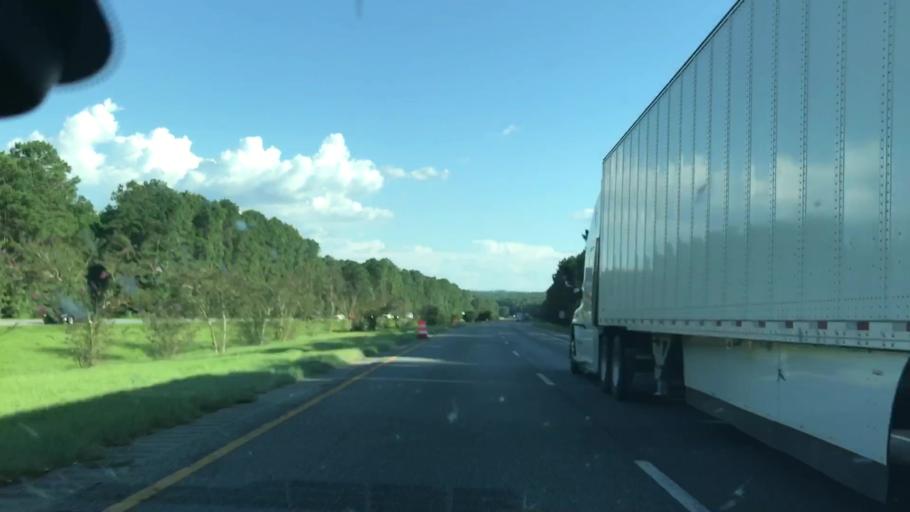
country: US
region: Georgia
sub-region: Harris County
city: Hamilton
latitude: 32.6508
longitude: -84.9730
